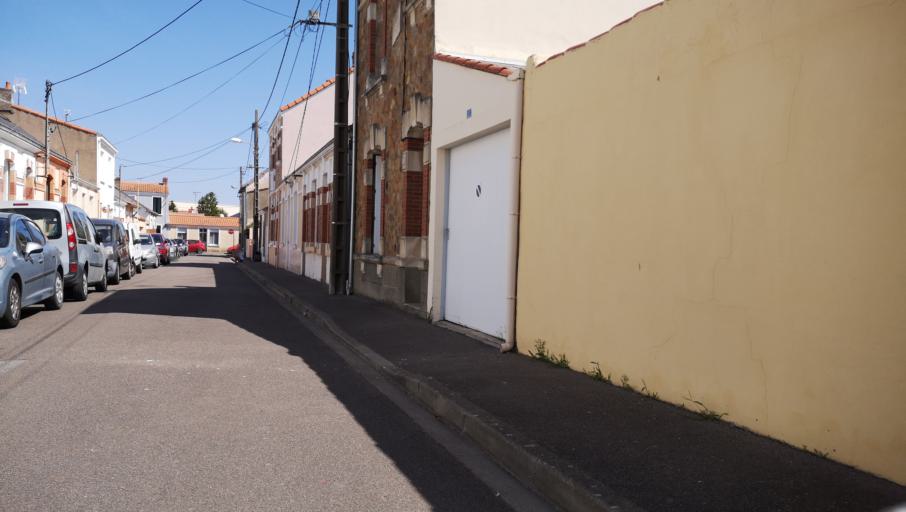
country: FR
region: Pays de la Loire
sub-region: Departement de la Vendee
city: Les Sables-d'Olonne
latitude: 46.4977
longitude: -1.7738
